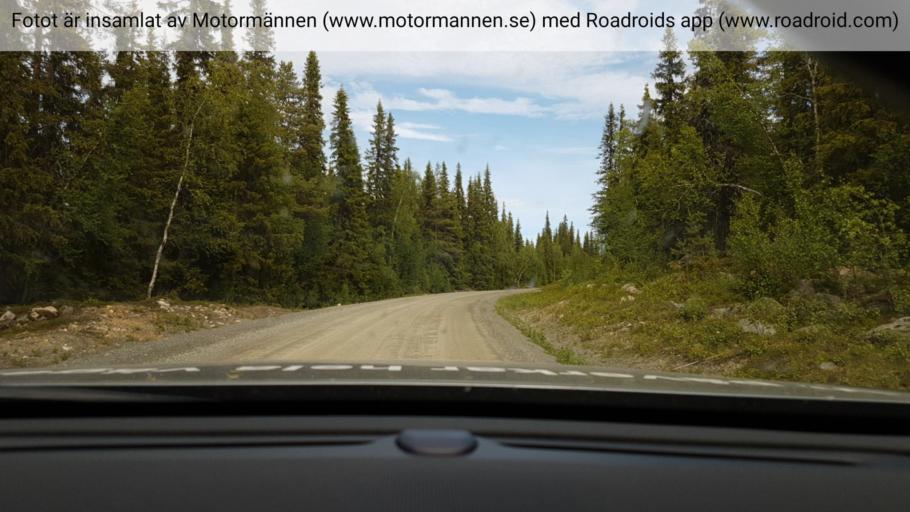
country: SE
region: Vaesterbotten
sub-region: Storumans Kommun
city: Fristad
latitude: 65.1765
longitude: 16.3670
